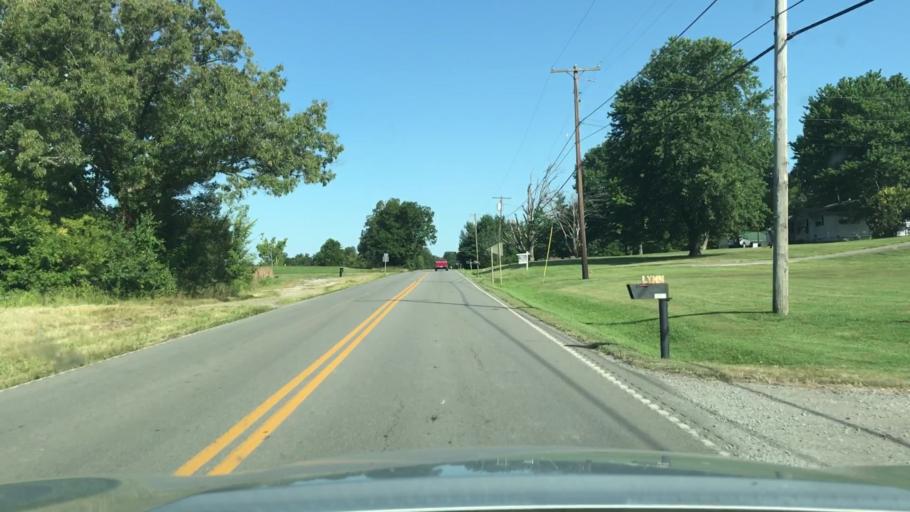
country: US
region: Kentucky
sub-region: Muhlenberg County
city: Greenville
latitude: 37.1828
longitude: -87.1565
